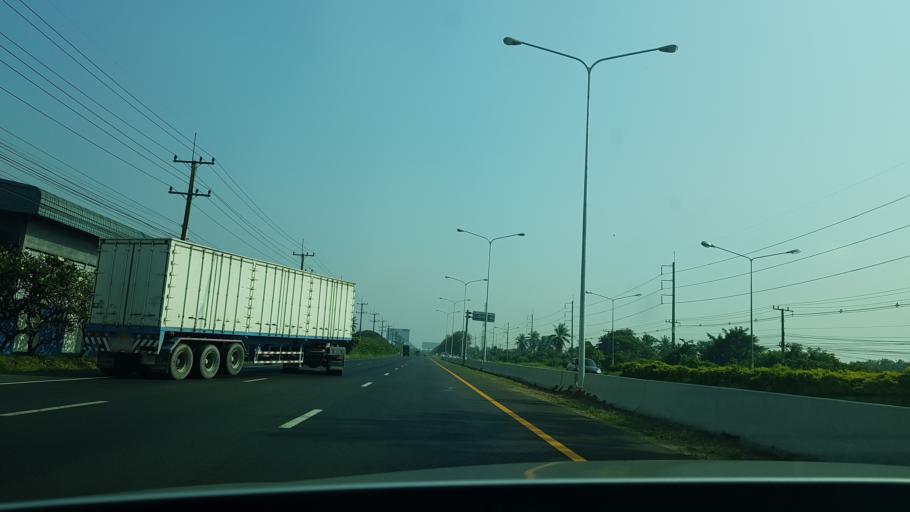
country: TH
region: Phetchaburi
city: Khao Yoi
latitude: 13.1787
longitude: 99.8368
